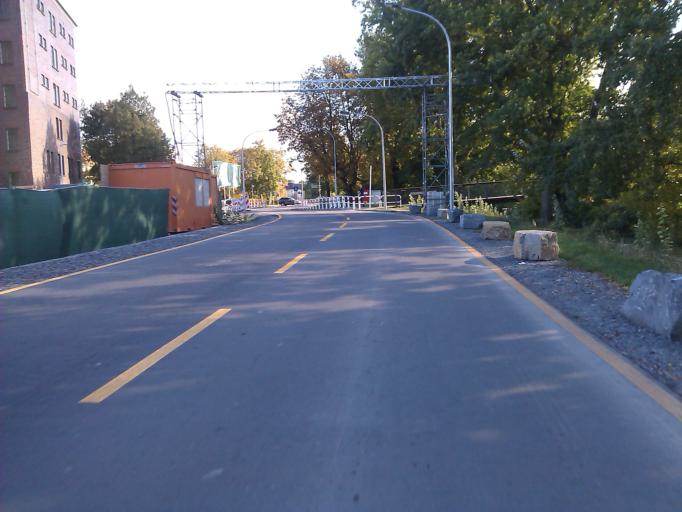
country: DE
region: Baden-Wuerttemberg
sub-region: Regierungsbezirk Stuttgart
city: Heilbronn
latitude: 49.1444
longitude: 9.2142
